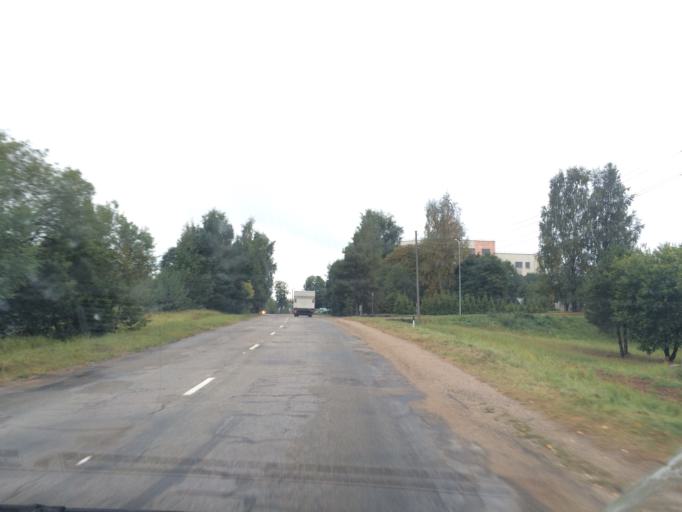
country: LV
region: Ikskile
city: Ikskile
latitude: 56.8443
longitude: 24.5024
